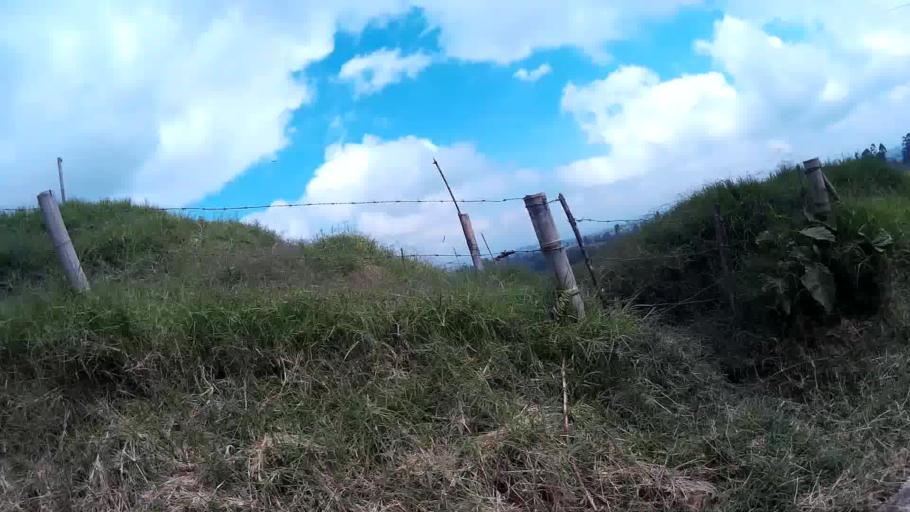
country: CO
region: Quindio
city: Filandia
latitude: 4.6810
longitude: -75.6584
